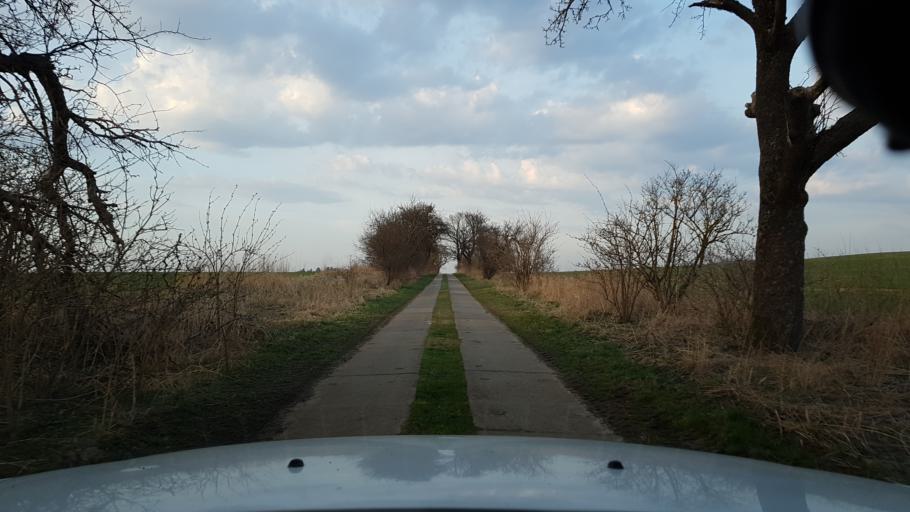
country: PL
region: West Pomeranian Voivodeship
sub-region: Koszalin
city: Koszalin
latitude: 54.0919
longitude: 16.1352
